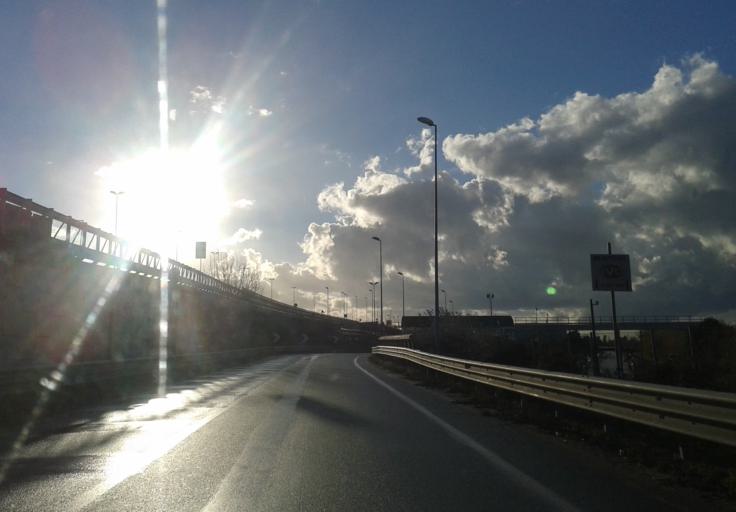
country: IT
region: Tuscany
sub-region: Provincia di Livorno
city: Livorno
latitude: 43.5864
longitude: 10.3169
